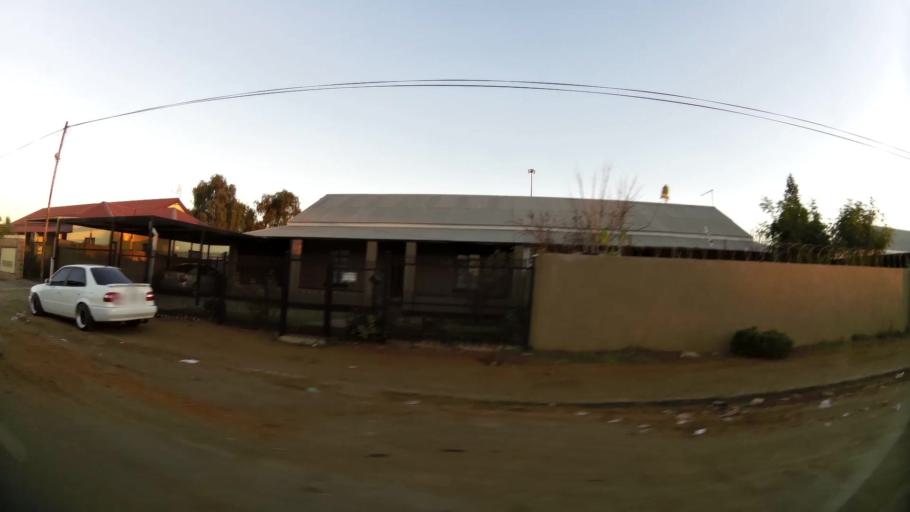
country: ZA
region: Northern Cape
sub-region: Frances Baard District Municipality
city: Kimberley
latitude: -28.7297
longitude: 24.7716
